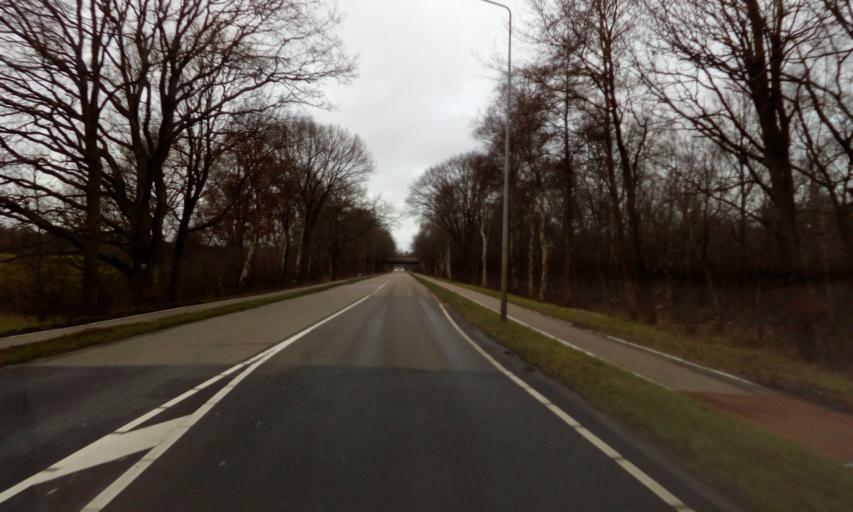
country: NL
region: North Holland
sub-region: Gemeente Bussum
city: Bussum
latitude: 52.2480
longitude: 5.1675
